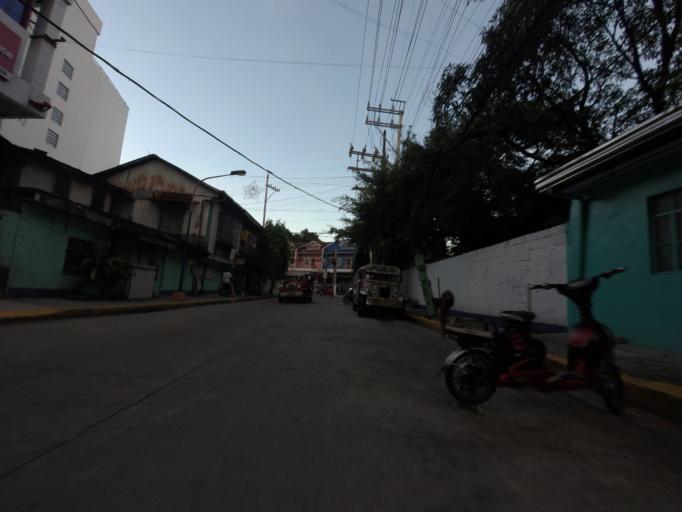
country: PH
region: Metro Manila
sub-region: City of Manila
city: Quiapo
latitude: 14.5962
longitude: 120.9914
